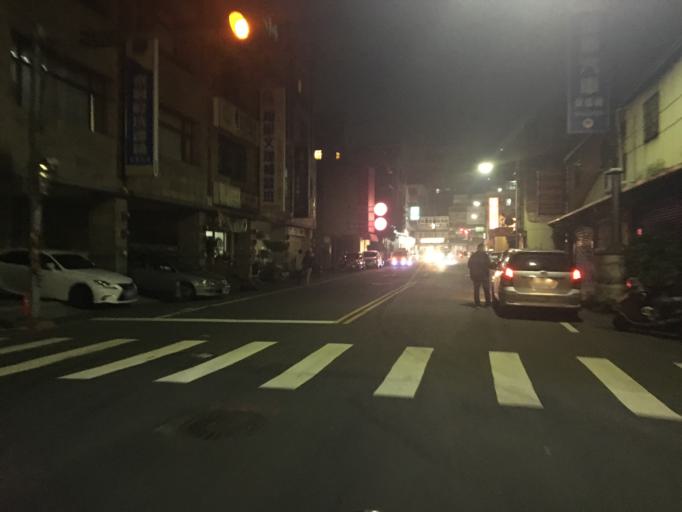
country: TW
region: Taiwan
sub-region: Hsinchu
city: Hsinchu
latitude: 24.8225
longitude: 120.9744
